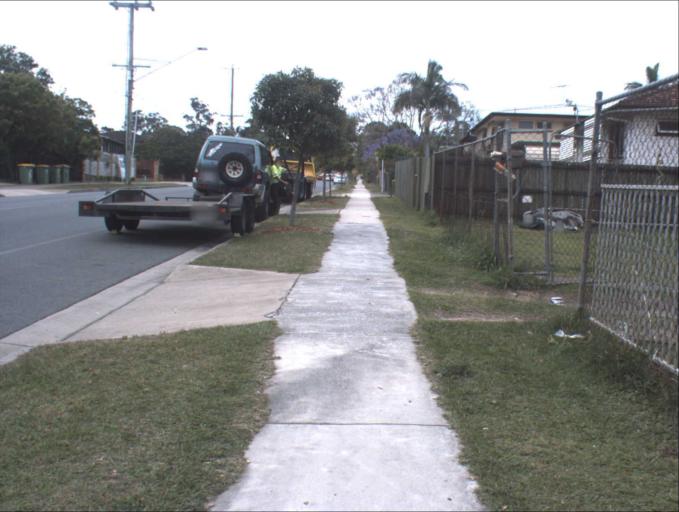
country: AU
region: Queensland
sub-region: Logan
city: Logan City
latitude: -27.6312
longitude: 153.1092
